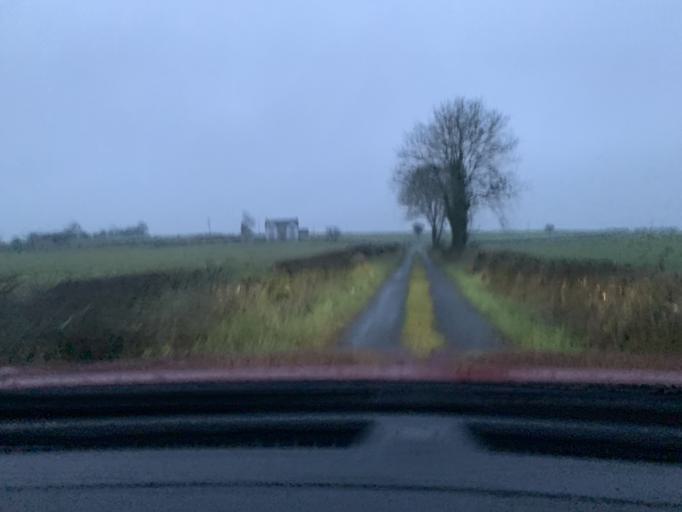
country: IE
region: Connaught
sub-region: Sligo
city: Ballymote
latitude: 54.0206
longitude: -8.5537
